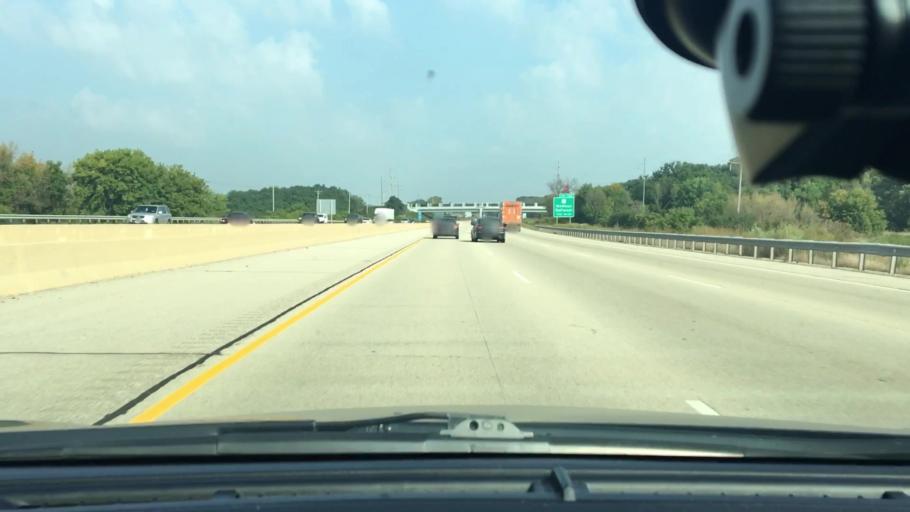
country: US
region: Wisconsin
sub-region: Dane County
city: Windsor
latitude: 43.1497
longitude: -89.3042
